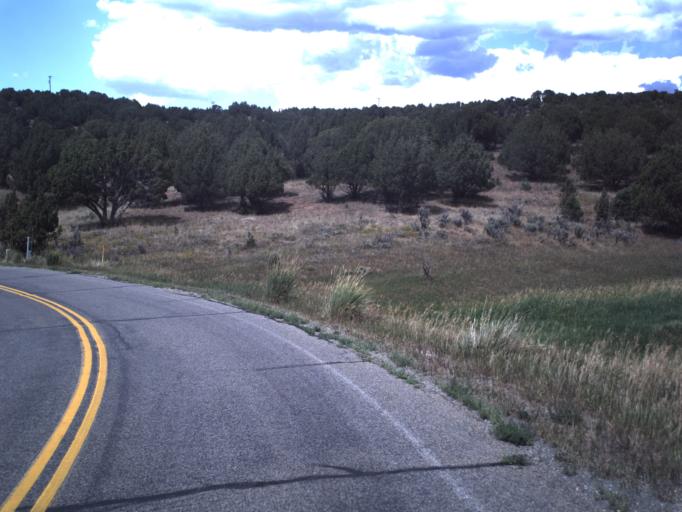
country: US
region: Utah
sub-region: Summit County
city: Oakley
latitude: 40.7682
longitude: -111.3855
